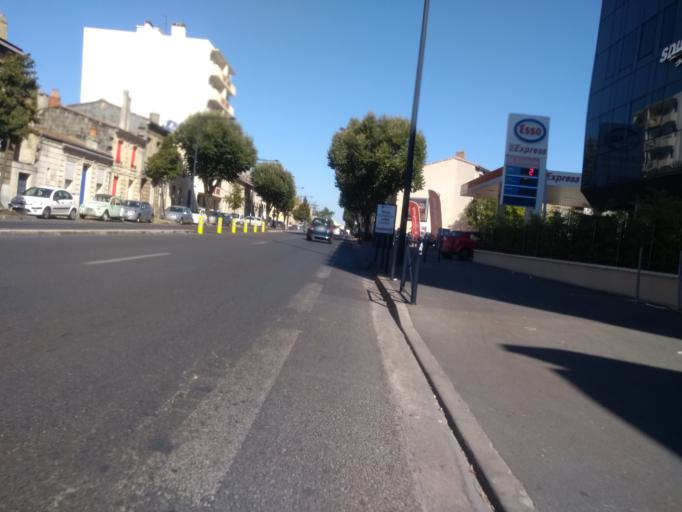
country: FR
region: Aquitaine
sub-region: Departement de la Gironde
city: Le Bouscat
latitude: 44.8549
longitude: -0.5926
